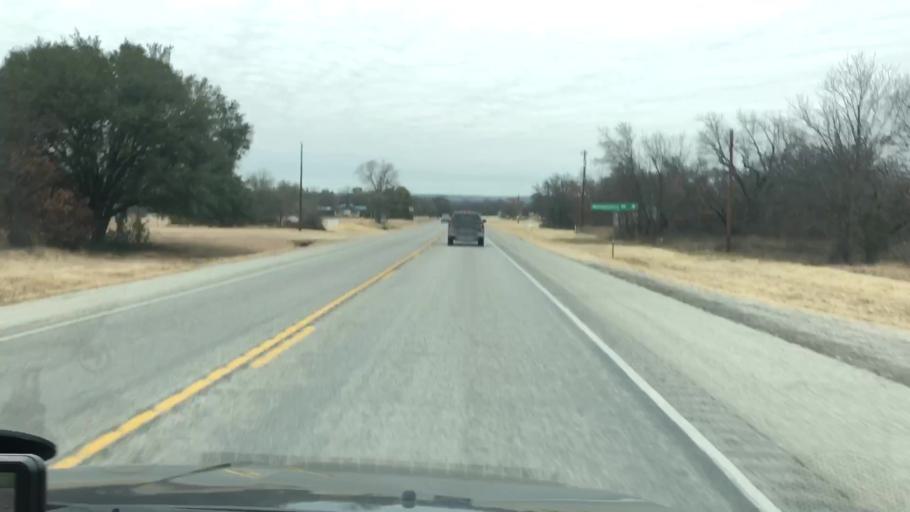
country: US
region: Texas
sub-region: Palo Pinto County
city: Mineral Wells
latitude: 32.8865
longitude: -98.0886
